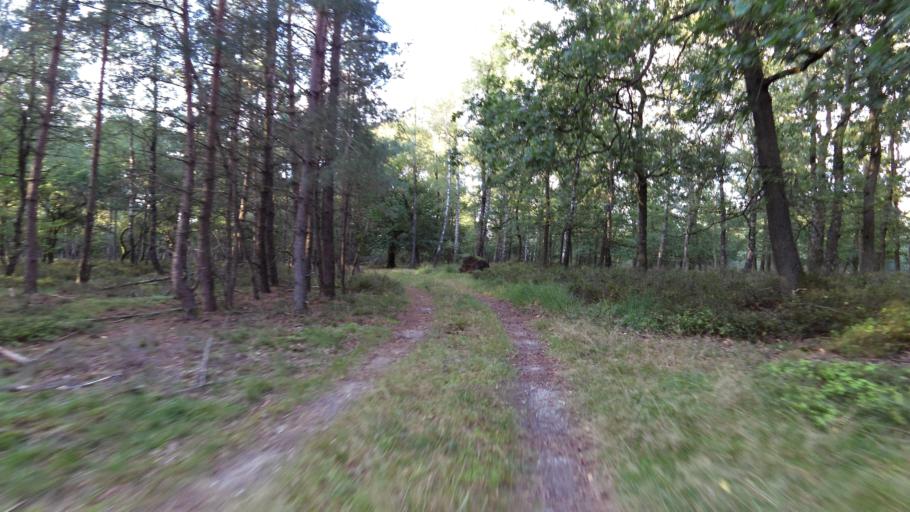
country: NL
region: Gelderland
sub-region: Gemeente Epe
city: Vaassen
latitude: 52.2974
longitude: 5.8743
